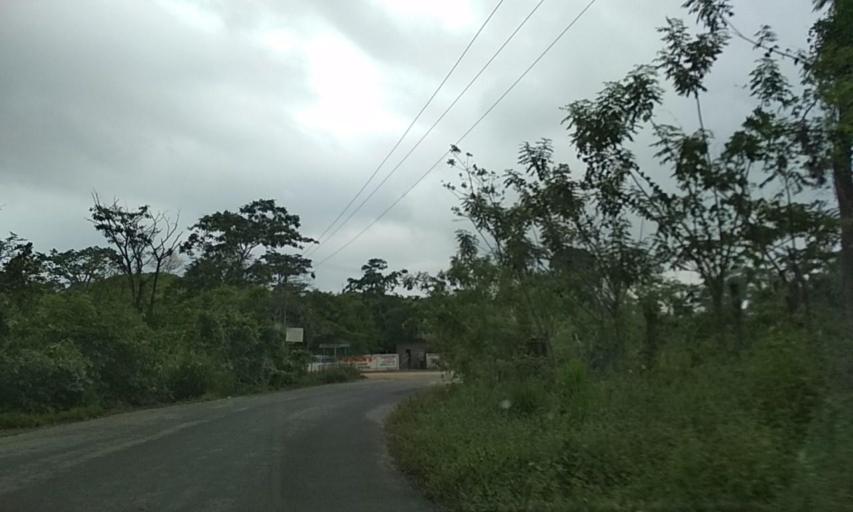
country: MX
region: Tabasco
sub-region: Huimanguillo
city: Francisco Rueda
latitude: 17.6439
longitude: -94.0941
